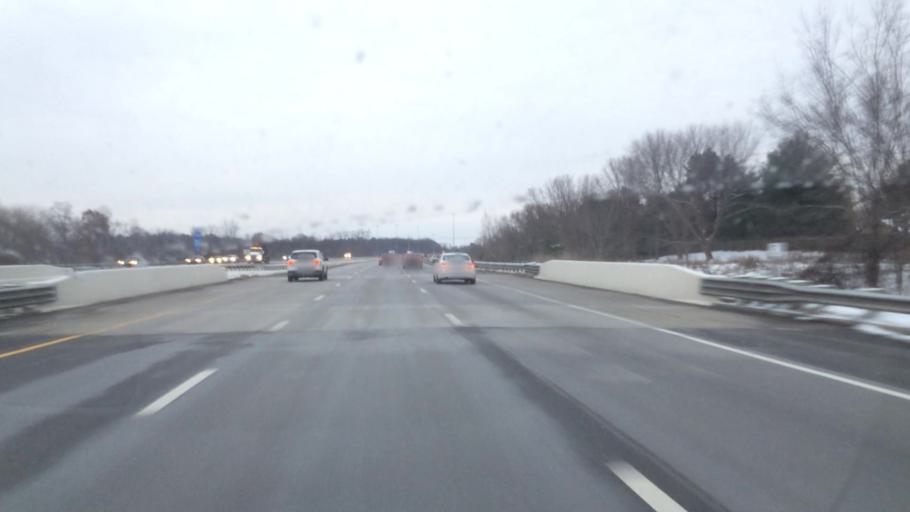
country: US
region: Ohio
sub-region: Medina County
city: Medina
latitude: 41.1692
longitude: -81.7860
